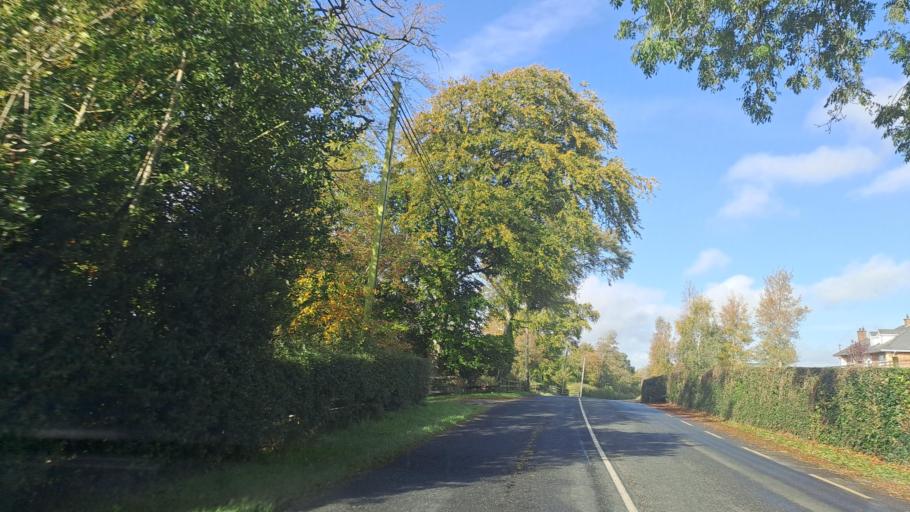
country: IE
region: Ulster
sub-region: An Cabhan
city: Bailieborough
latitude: 54.0065
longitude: -6.9191
